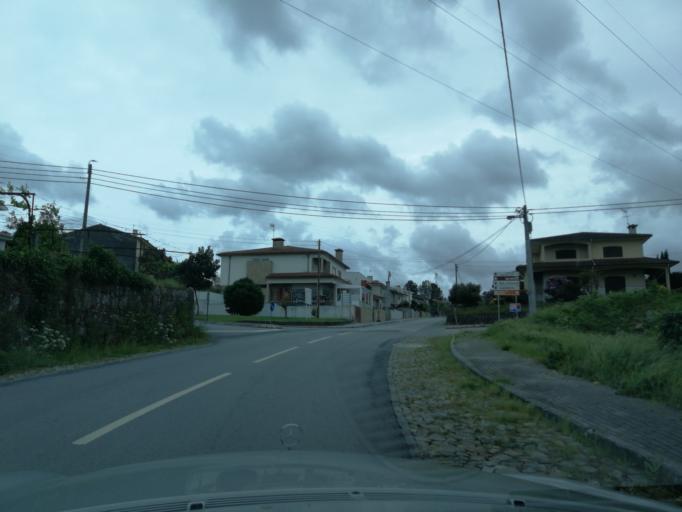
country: PT
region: Braga
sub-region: Braga
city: Adaufe
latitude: 41.6057
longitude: -8.3827
